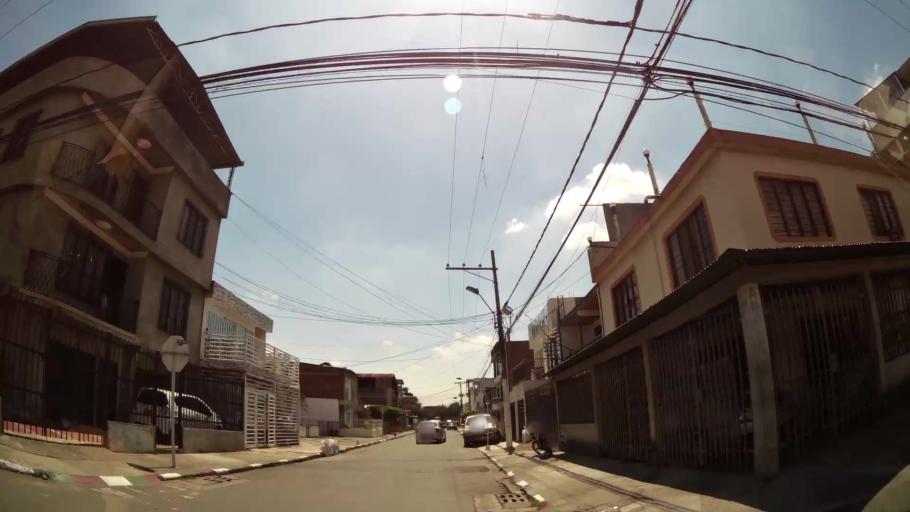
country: CO
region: Valle del Cauca
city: Cali
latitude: 3.4355
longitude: -76.4972
